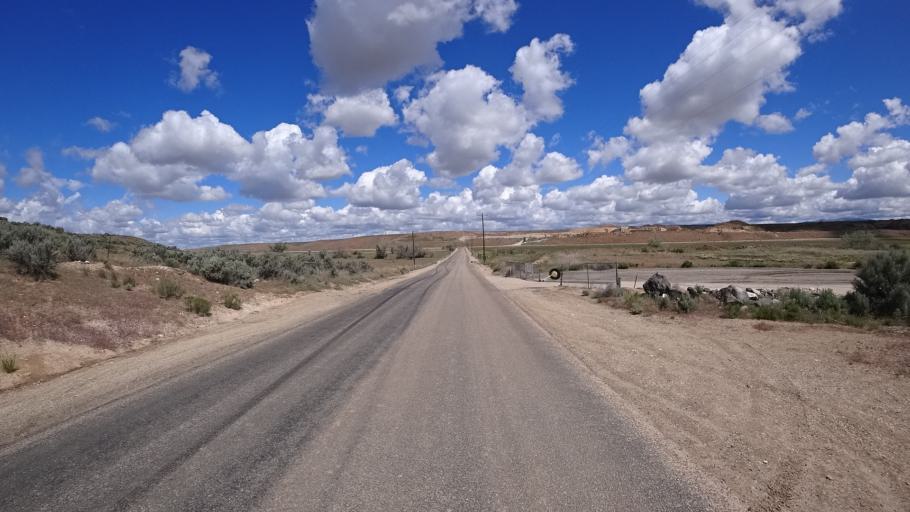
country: US
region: Idaho
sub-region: Ada County
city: Garden City
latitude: 43.4886
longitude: -116.2743
